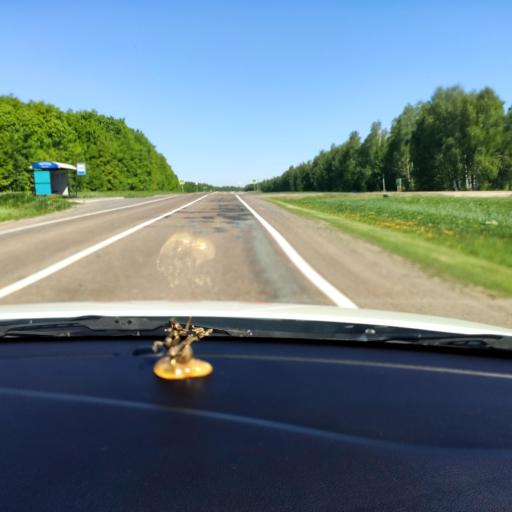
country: RU
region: Tatarstan
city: Vysokaya Gora
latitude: 56.0796
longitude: 49.1871
